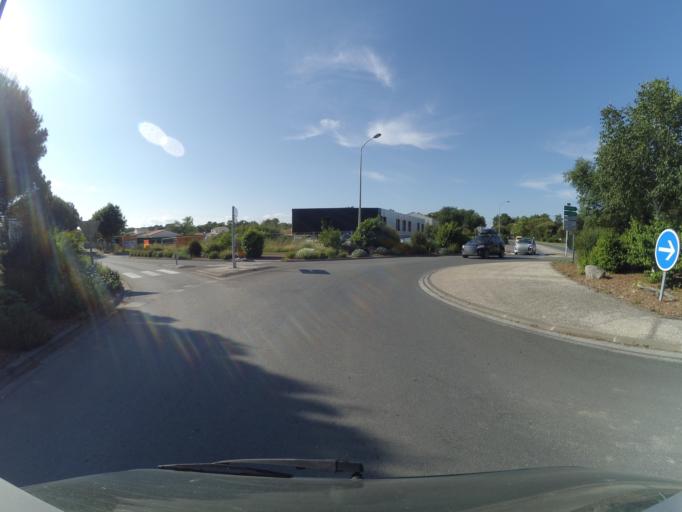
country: FR
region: Poitou-Charentes
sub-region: Departement de la Charente-Maritime
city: Saint-Sulpice-de-Royan
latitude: 45.6533
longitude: -1.0232
